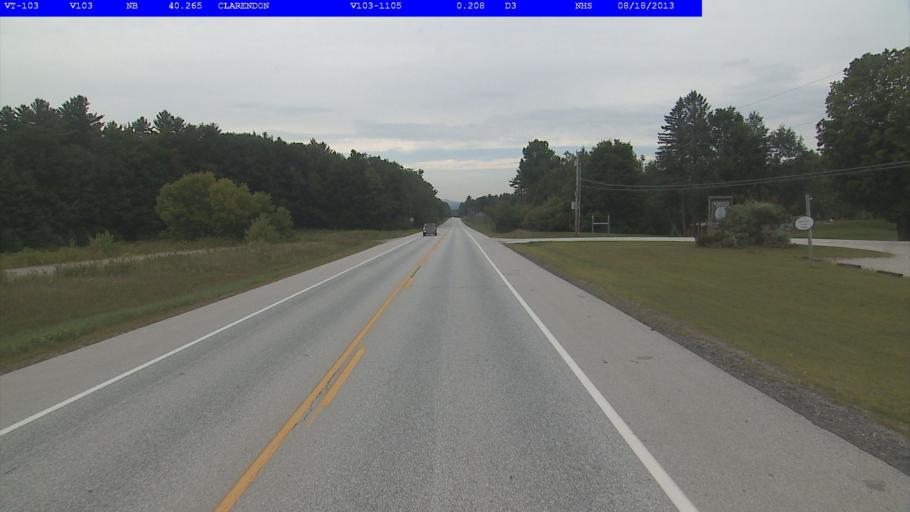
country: US
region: Vermont
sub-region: Rutland County
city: Rutland
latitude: 43.5262
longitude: -72.9333
